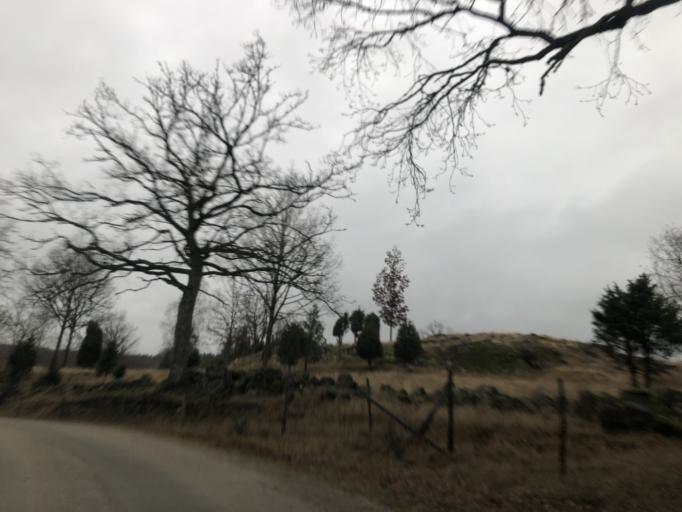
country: SE
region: Vaestra Goetaland
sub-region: Ulricehamns Kommun
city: Ulricehamn
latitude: 57.7957
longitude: 13.3869
